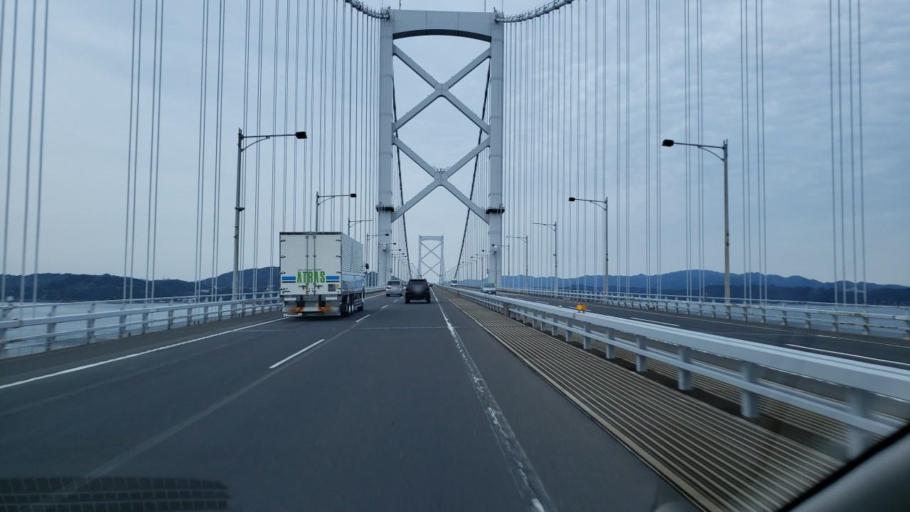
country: JP
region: Tokushima
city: Narutocho-mitsuishi
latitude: 34.2360
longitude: 134.6442
